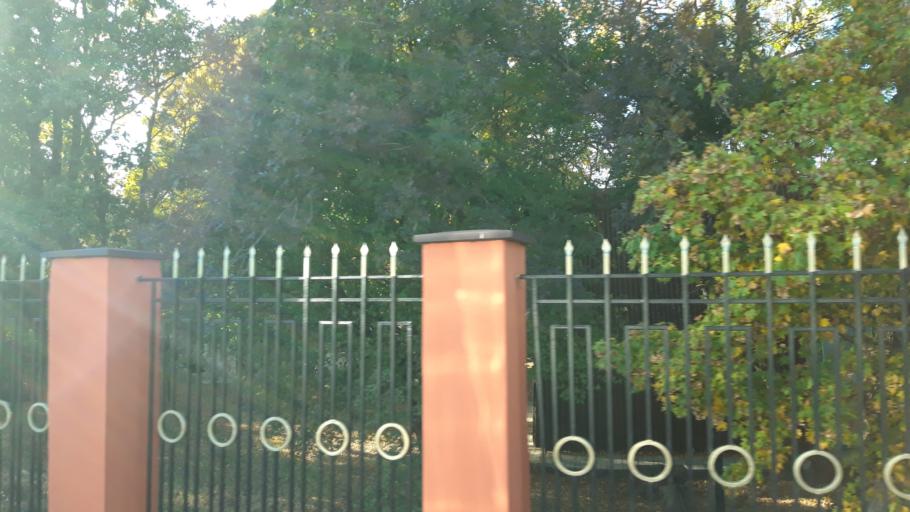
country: RU
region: Krasnodarskiy
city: Kabardinka
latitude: 44.6465
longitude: 37.9385
